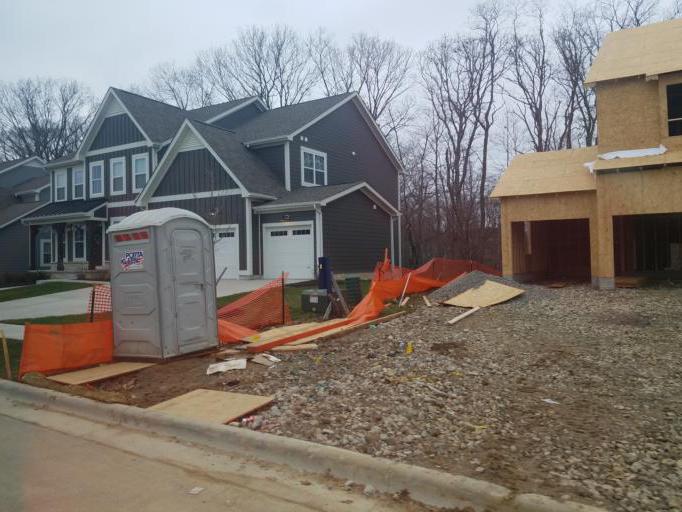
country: US
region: Ohio
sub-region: Franklin County
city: Westerville
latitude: 40.1321
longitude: -82.9582
